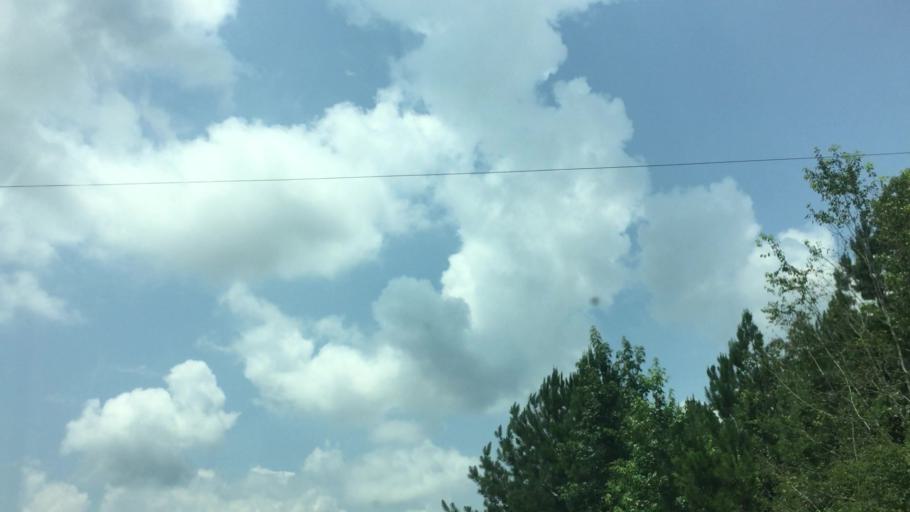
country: US
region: Georgia
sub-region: Fulton County
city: Chattahoochee Hills
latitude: 33.5784
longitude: -84.8035
